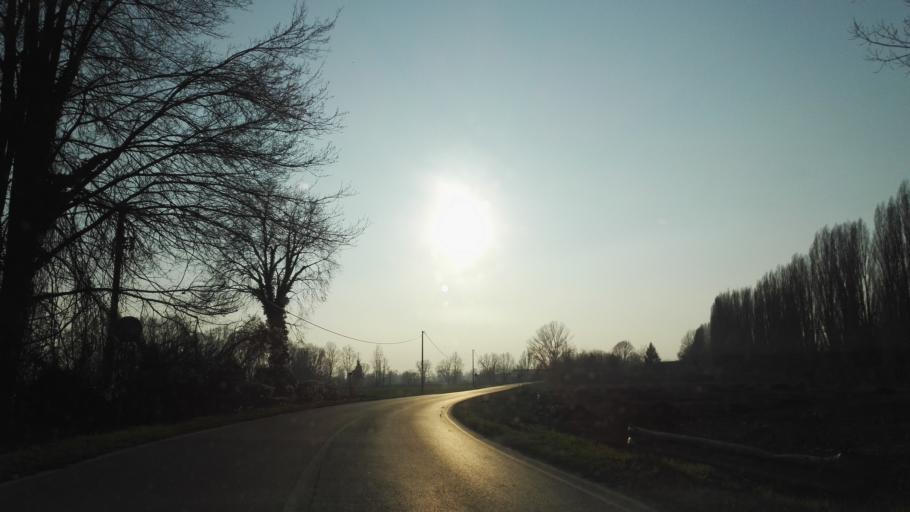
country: IT
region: Lombardy
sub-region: Citta metropolitana di Milano
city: Tribiano
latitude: 45.4041
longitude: 9.3670
